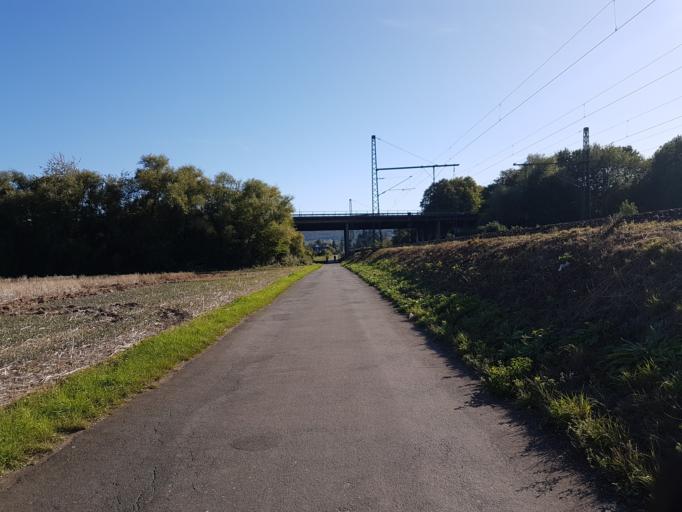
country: DE
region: North Rhine-Westphalia
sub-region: Regierungsbezirk Detmold
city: Minden
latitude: 52.2736
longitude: 8.9330
